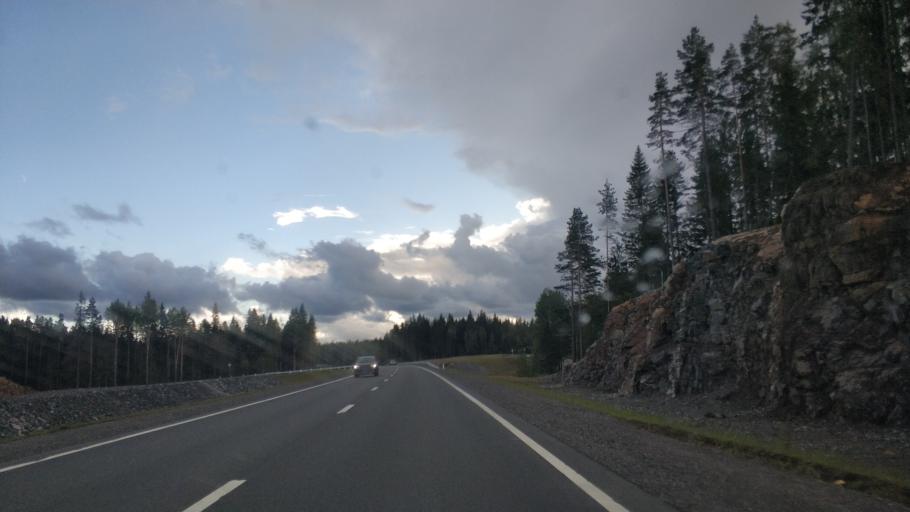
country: RU
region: Republic of Karelia
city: Lakhdenpokh'ya
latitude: 61.4231
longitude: 29.9649
